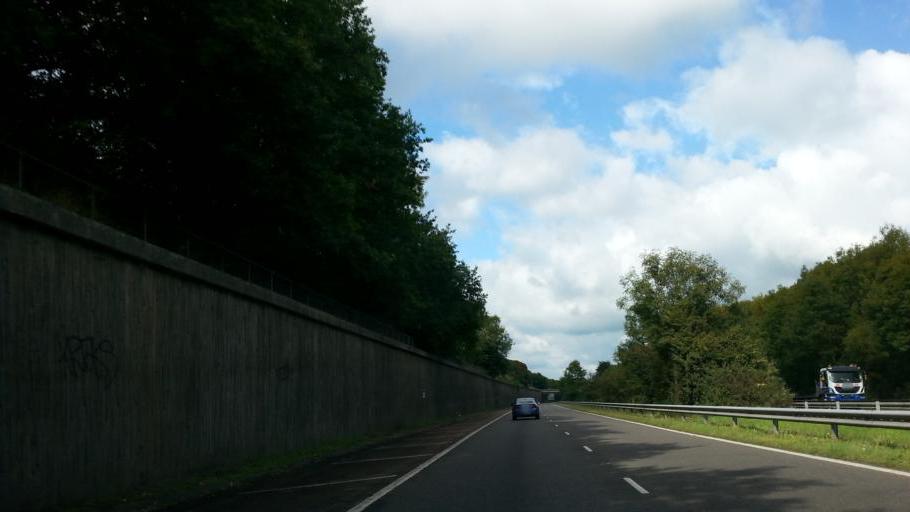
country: GB
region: England
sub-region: Wokingham
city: Earley
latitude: 51.4432
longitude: -0.9224
